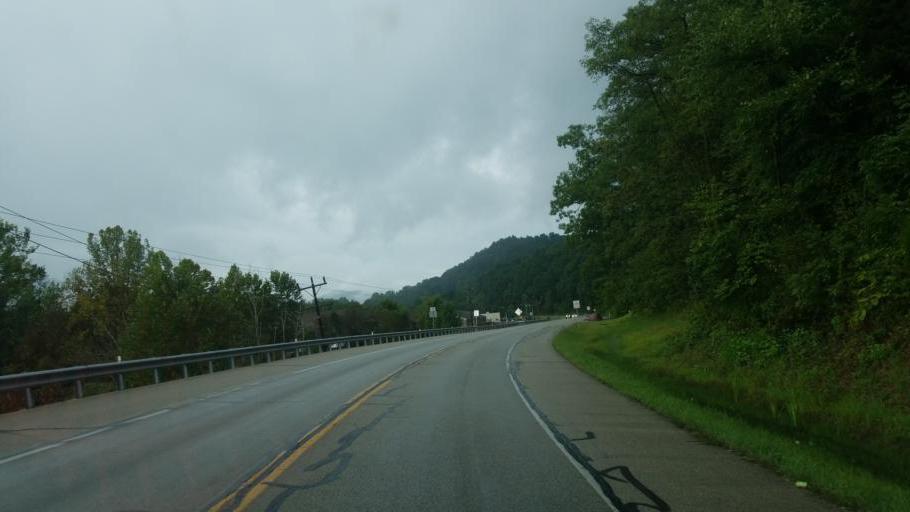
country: US
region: Kentucky
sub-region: Rowan County
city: Morehead
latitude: 38.1678
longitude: -83.4409
